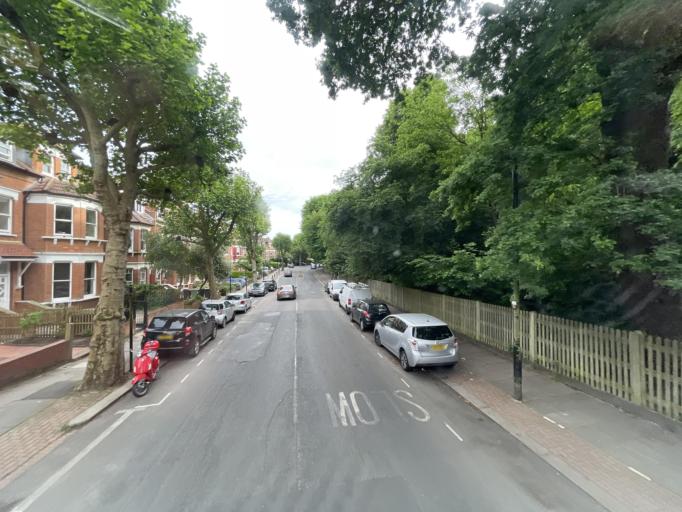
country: GB
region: England
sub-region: Greater London
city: Crouch End
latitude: 51.5834
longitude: -0.1466
